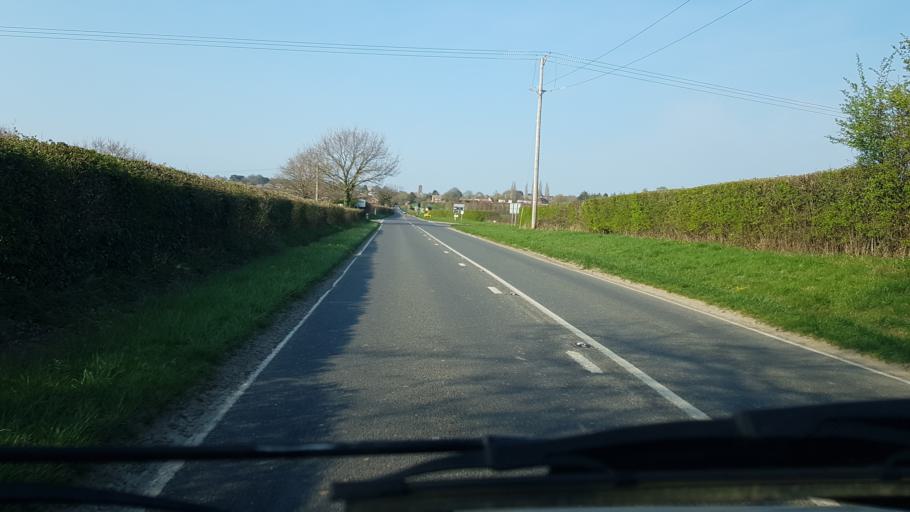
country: GB
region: England
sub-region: West Sussex
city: Petworth
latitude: 50.9745
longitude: -0.6136
